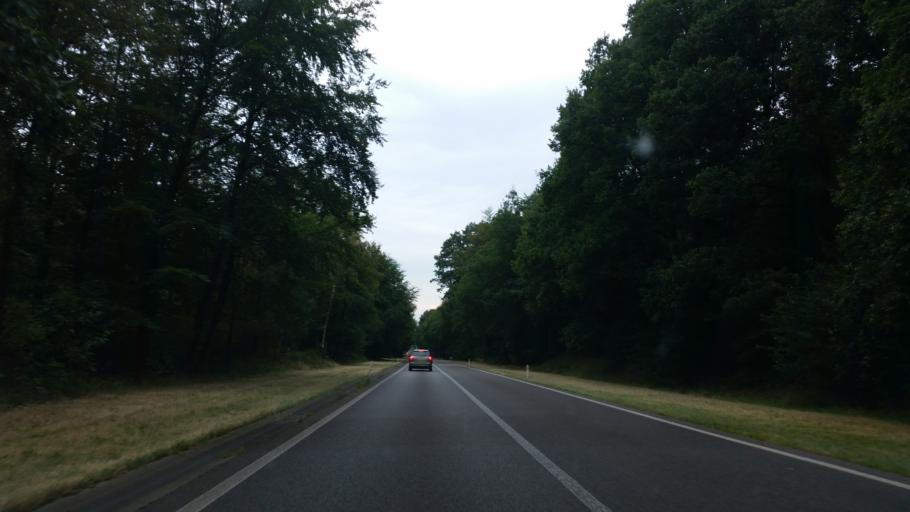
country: NL
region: Gelderland
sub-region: Gemeente Ede
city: Ede
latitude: 52.0603
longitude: 5.6833
